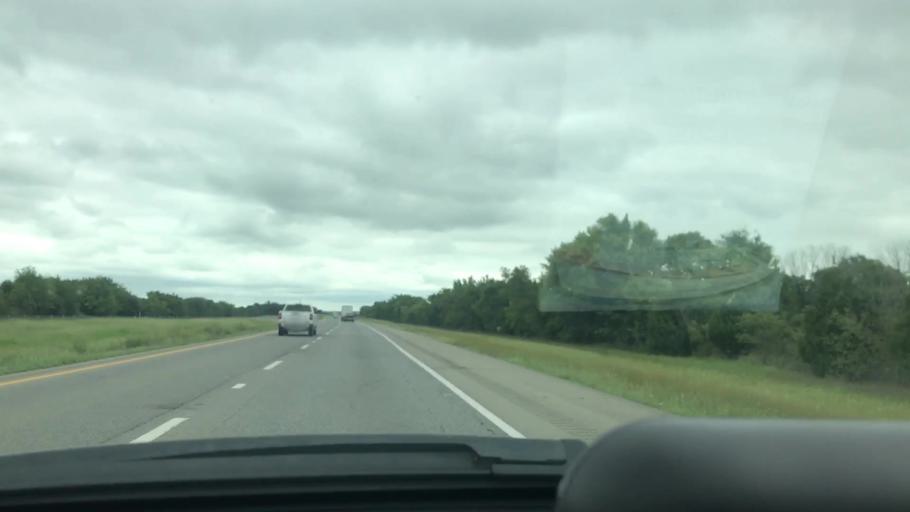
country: US
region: Oklahoma
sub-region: McIntosh County
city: Eufaula
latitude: 35.3798
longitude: -95.5684
